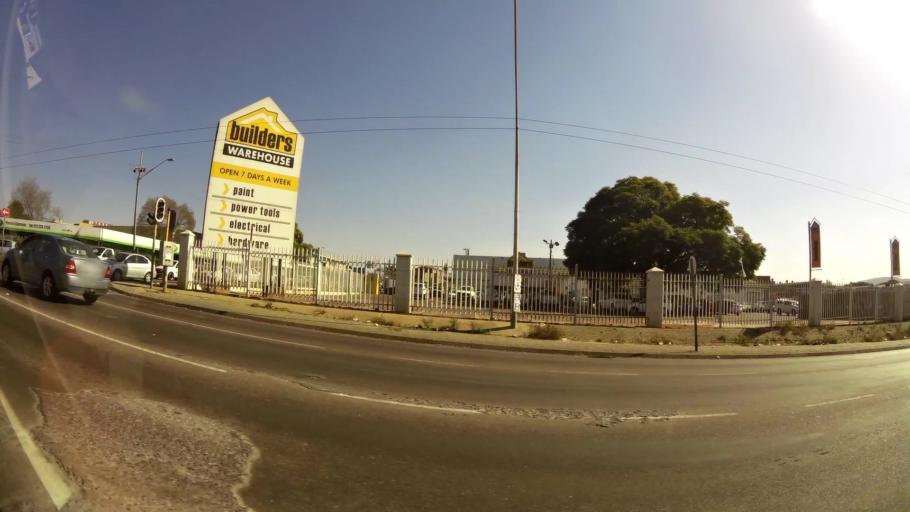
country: ZA
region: Gauteng
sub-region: City of Tshwane Metropolitan Municipality
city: Pretoria
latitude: -25.7246
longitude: 28.2051
